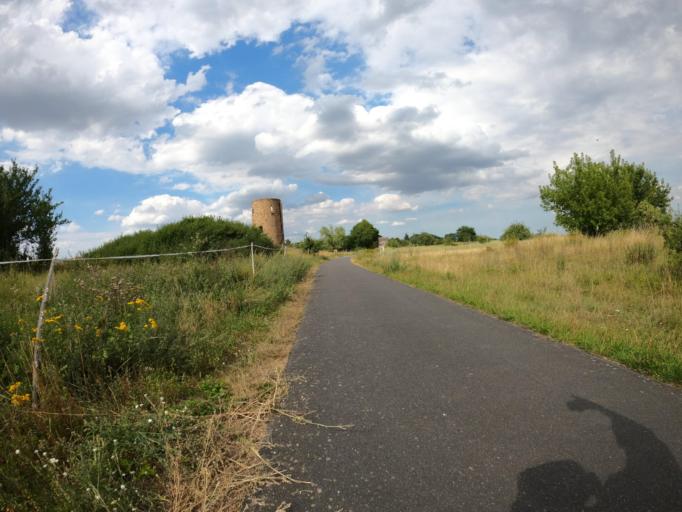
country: DE
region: Mecklenburg-Vorpommern
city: Woldegk
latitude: 53.3876
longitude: 13.5912
